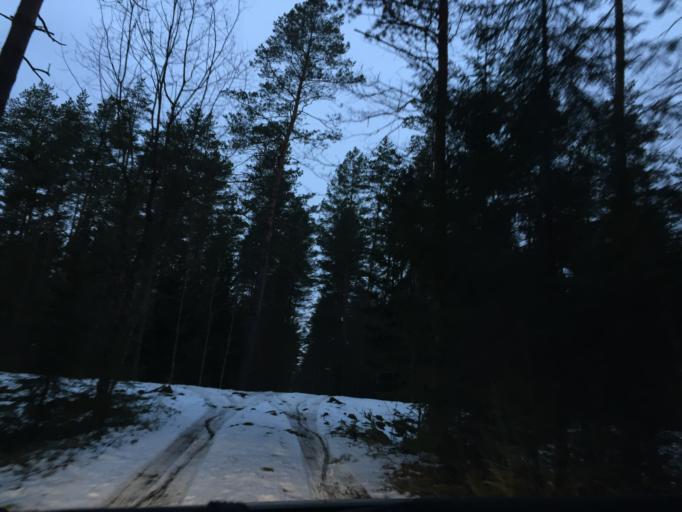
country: LV
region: Garkalne
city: Garkalne
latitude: 56.9665
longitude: 24.4680
